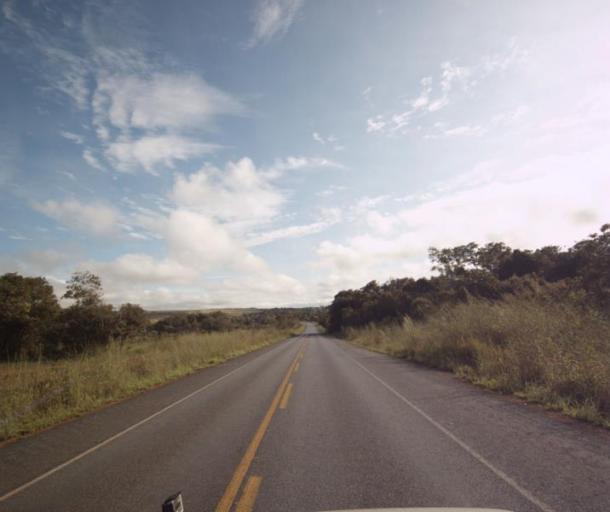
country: BR
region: Goias
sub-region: Padre Bernardo
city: Padre Bernardo
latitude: -15.4954
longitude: -48.6193
